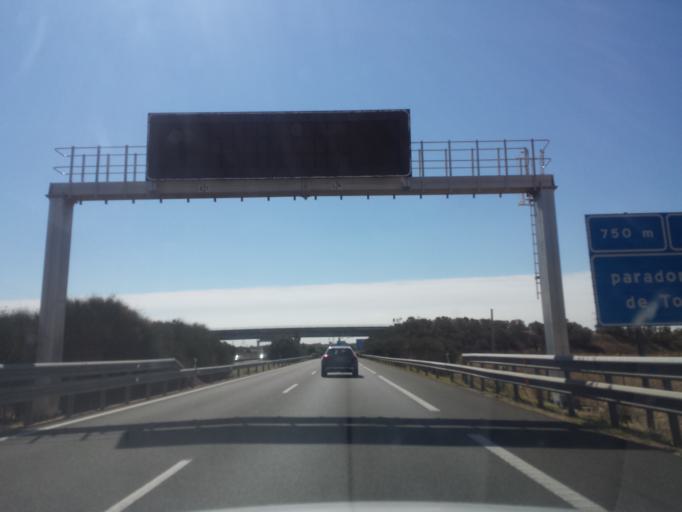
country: ES
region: Castille and Leon
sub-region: Provincia de Valladolid
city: Tordesillas
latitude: 41.5178
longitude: -5.0306
